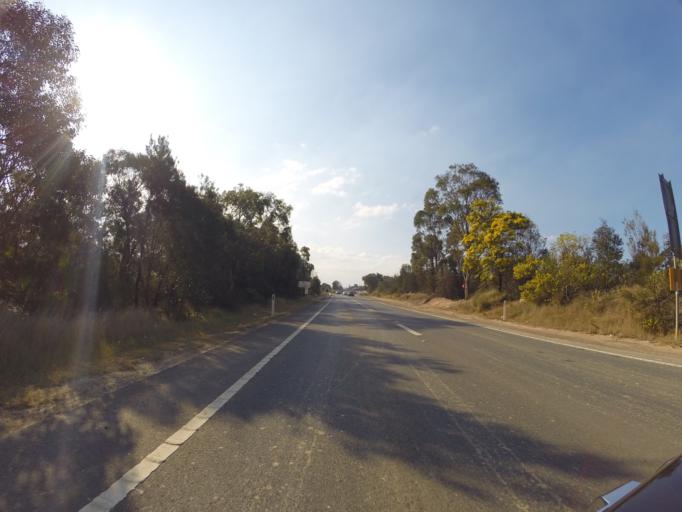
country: AU
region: New South Wales
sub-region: Sutherland Shire
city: Menai
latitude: -33.9945
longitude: 150.9967
